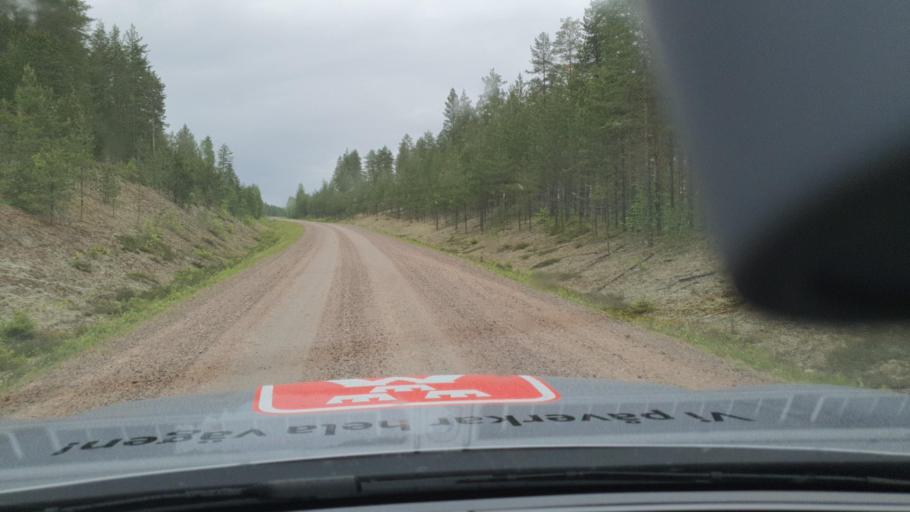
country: SE
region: Norrbotten
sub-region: Overkalix Kommun
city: OEverkalix
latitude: 66.5674
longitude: 22.7499
